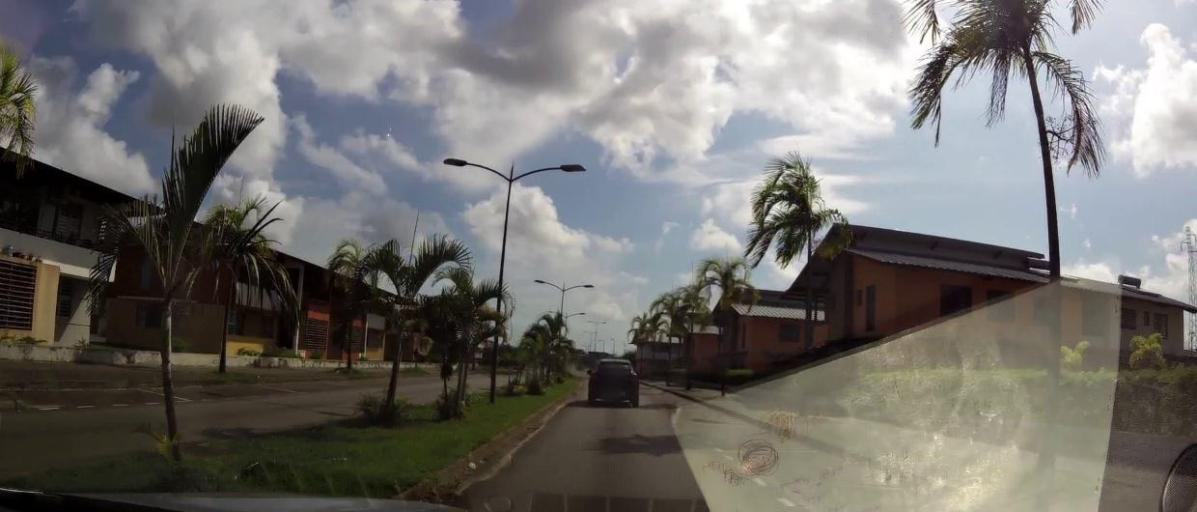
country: GF
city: Macouria
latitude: 4.9254
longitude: -52.4144
